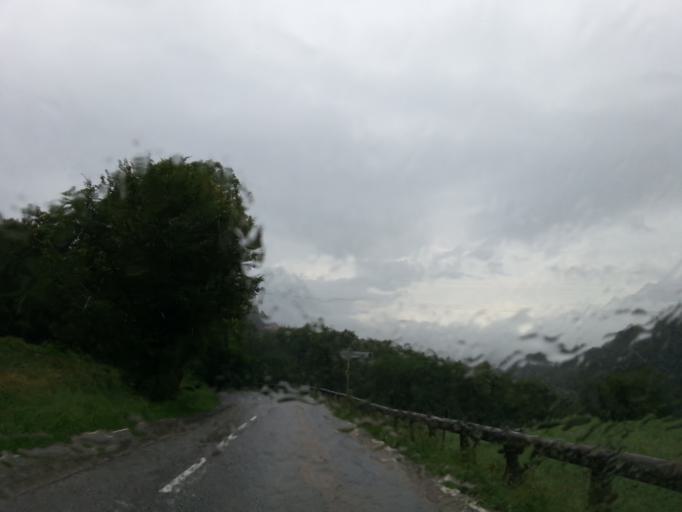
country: FR
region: Rhone-Alpes
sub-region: Departement de la Savoie
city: Albertville
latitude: 45.6901
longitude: 6.4061
